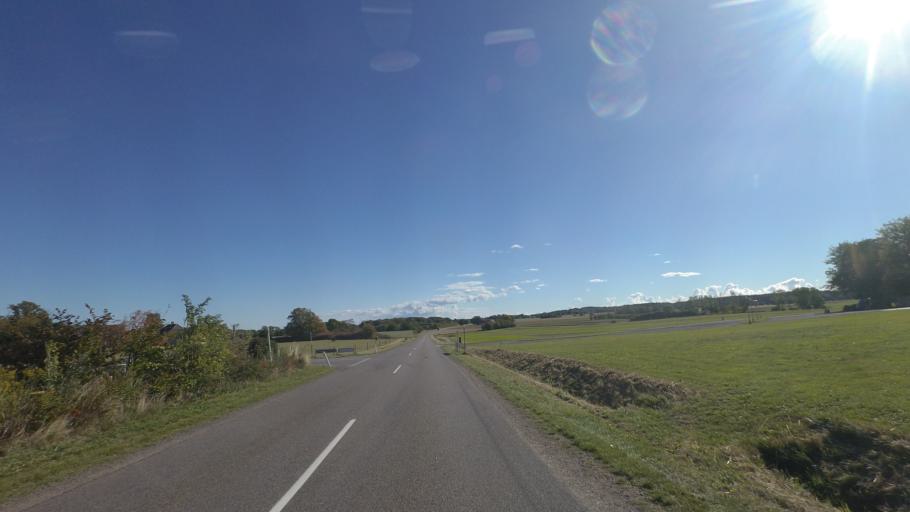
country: DK
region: Capital Region
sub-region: Bornholm Kommune
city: Nexo
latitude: 55.1174
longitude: 15.1059
